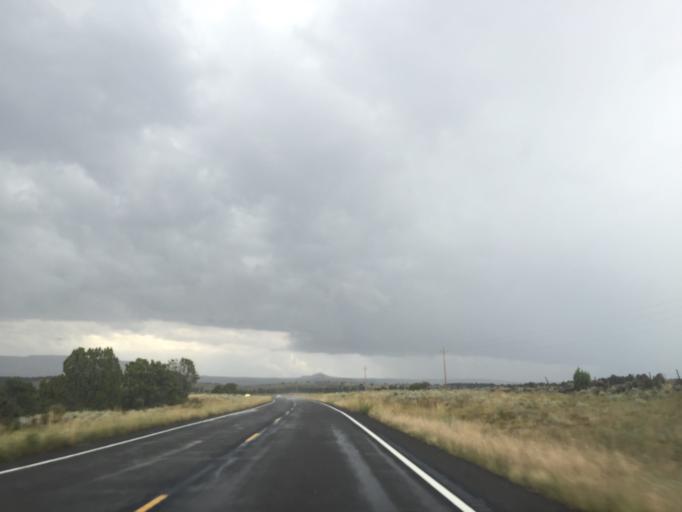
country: US
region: Utah
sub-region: Kane County
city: Kanab
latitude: 37.2395
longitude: -112.7489
